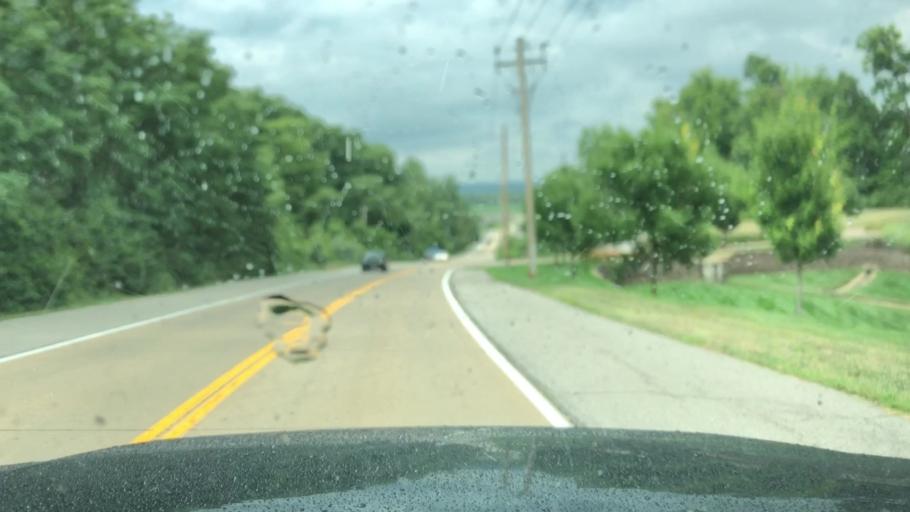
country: US
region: Missouri
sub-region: Saint Charles County
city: Saint Peters
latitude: 38.8004
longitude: -90.5806
